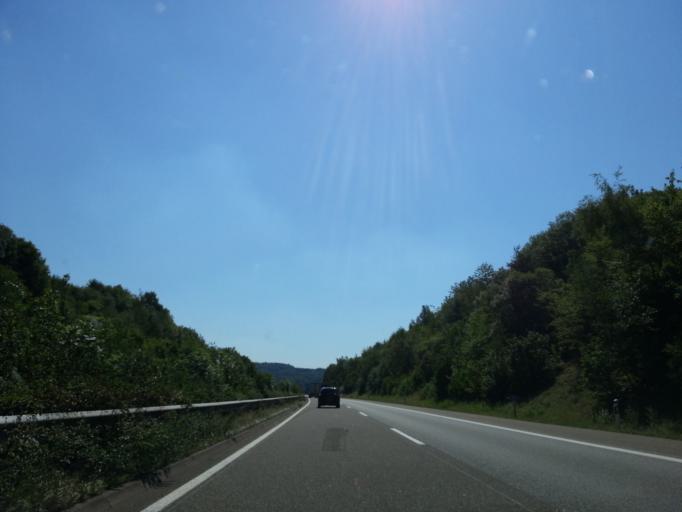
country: DE
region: Rheinland-Pfalz
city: Bickendorf
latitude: 50.0459
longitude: 6.4969
